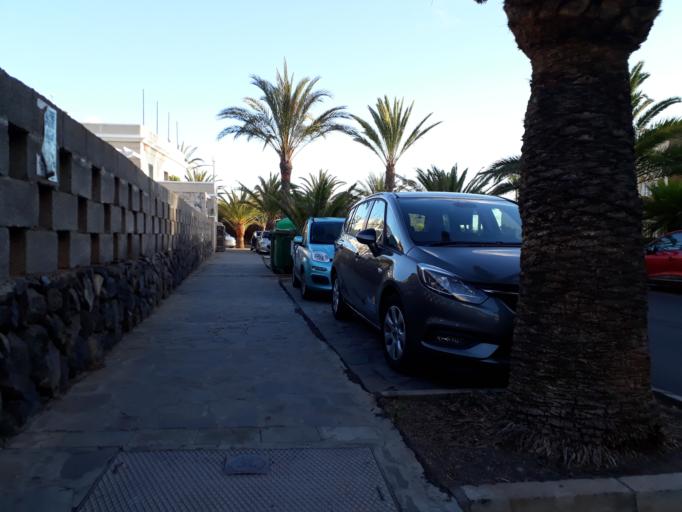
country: ES
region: Canary Islands
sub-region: Provincia de Santa Cruz de Tenerife
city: Alajero
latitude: 28.0868
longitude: -17.3386
